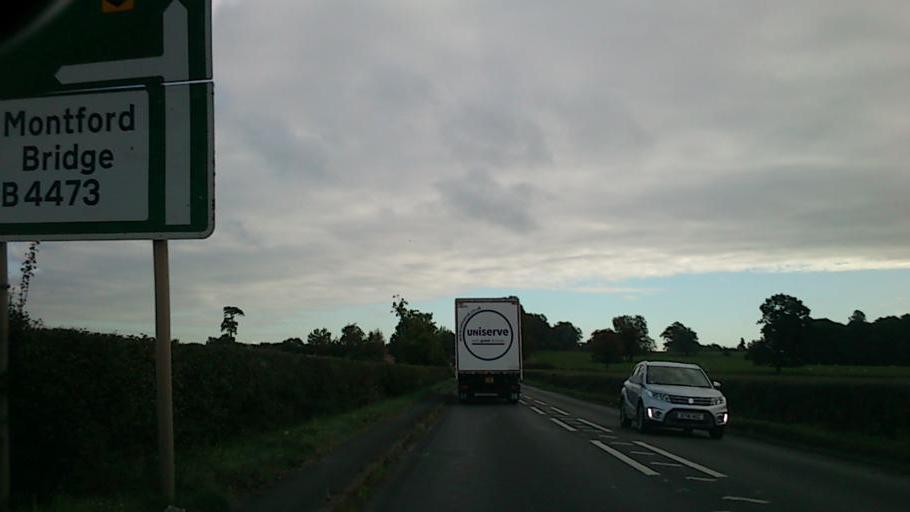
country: GB
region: England
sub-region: Shropshire
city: Ford
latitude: 52.7152
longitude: -2.8468
